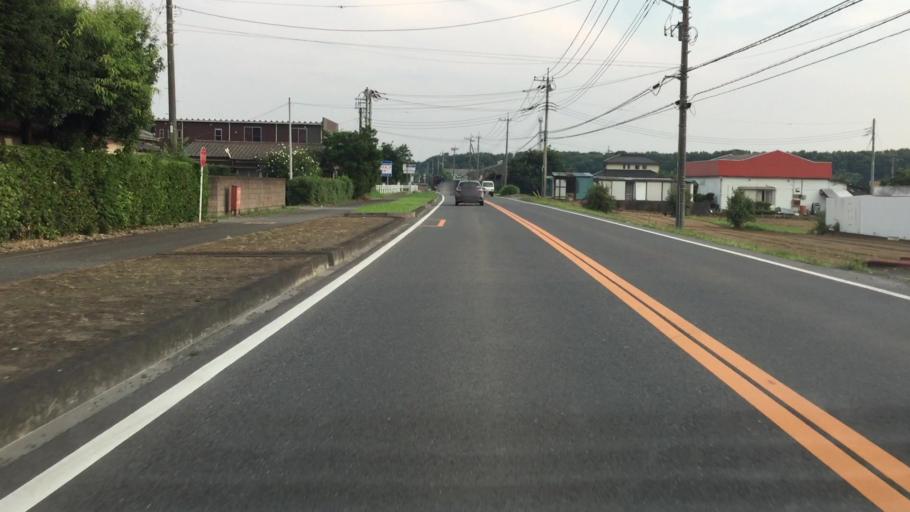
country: JP
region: Tochigi
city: Fujioka
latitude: 36.3051
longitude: 139.6707
